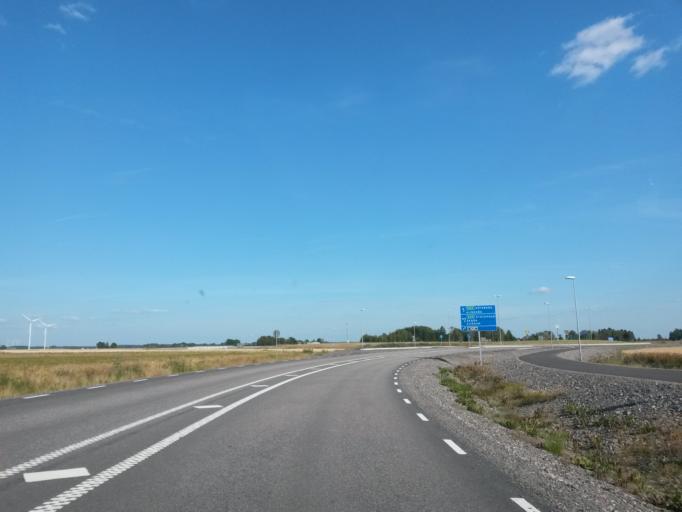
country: SE
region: Vaestra Goetaland
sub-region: Vara Kommun
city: Kvanum
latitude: 58.3301
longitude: 13.1311
